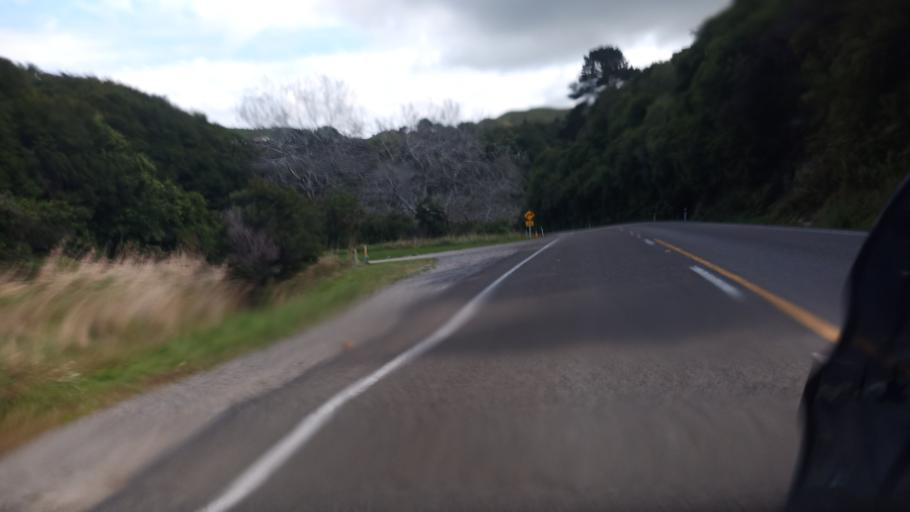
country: NZ
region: Gisborne
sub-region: Gisborne District
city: Gisborne
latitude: -38.4341
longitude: 178.2739
